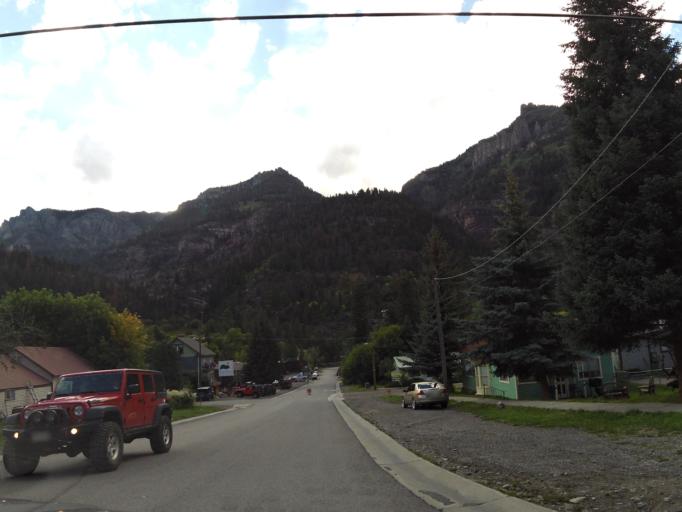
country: US
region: Colorado
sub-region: Ouray County
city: Ouray
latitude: 38.0195
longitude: -107.6722
